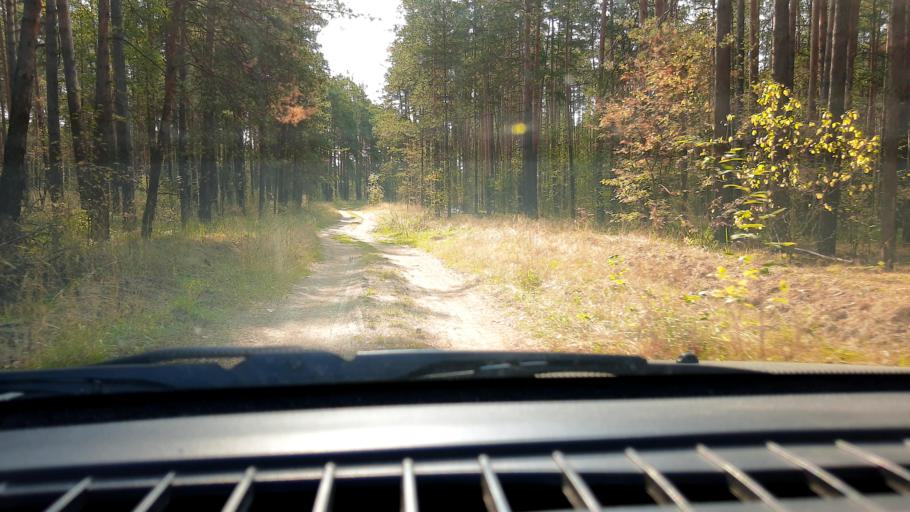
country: RU
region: Nizjnij Novgorod
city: Lukino
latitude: 56.3978
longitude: 43.6430
